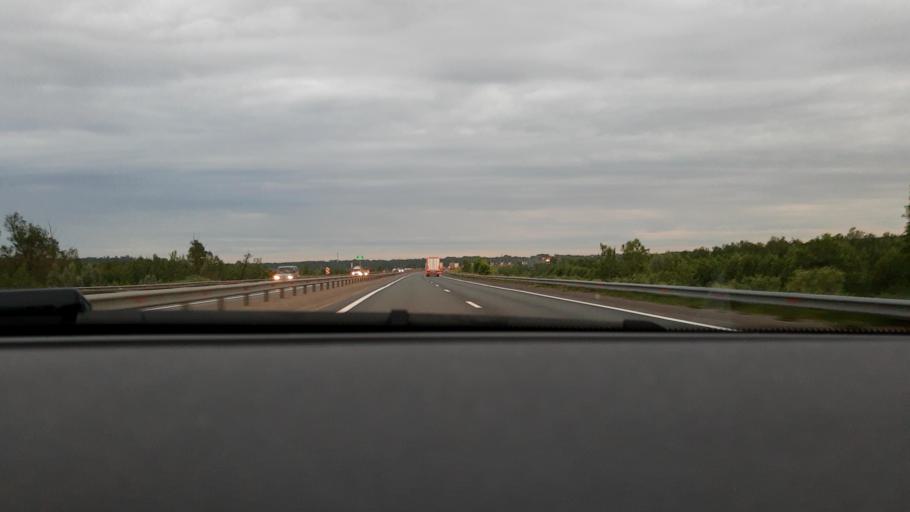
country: RU
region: Nizjnij Novgorod
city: Gorbatovka
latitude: 56.2014
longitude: 43.7522
